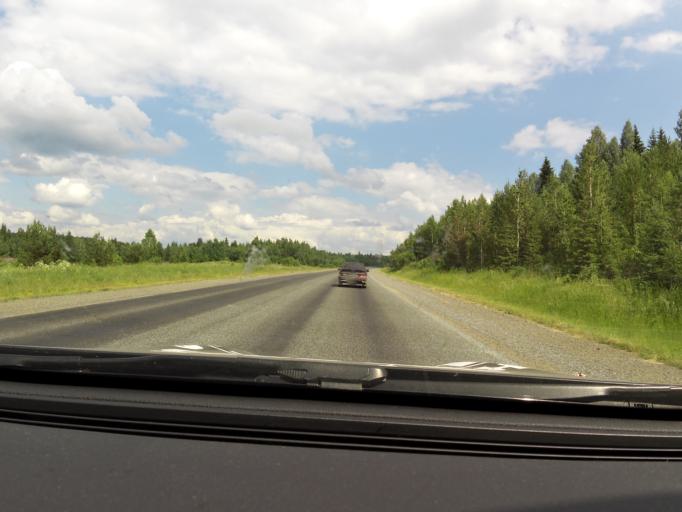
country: RU
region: Sverdlovsk
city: Arti
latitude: 56.7951
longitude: 58.4678
